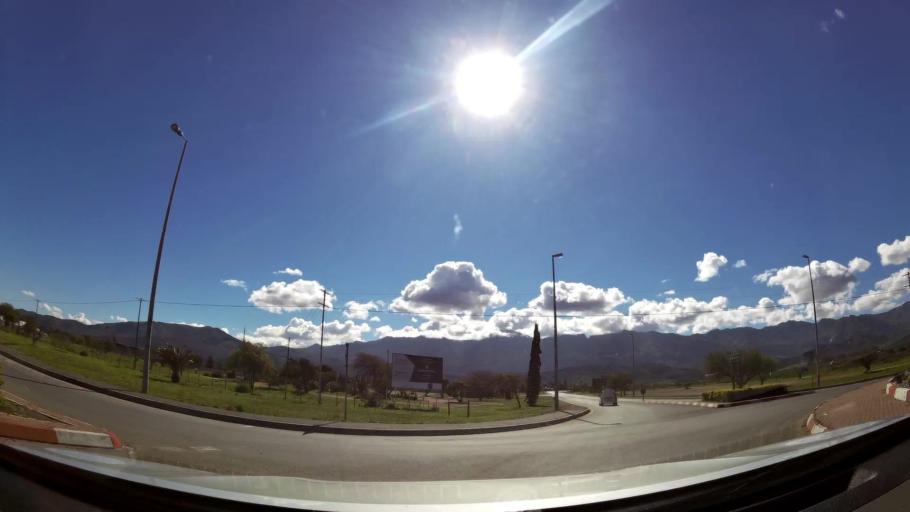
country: ZA
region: Western Cape
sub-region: Cape Winelands District Municipality
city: Ashton
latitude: -33.8150
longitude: 19.8976
